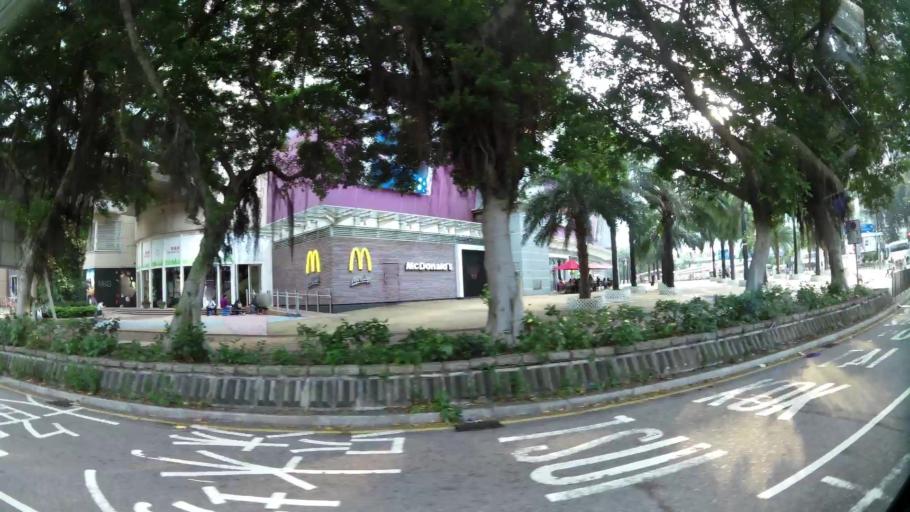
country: HK
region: Sham Shui Po
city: Sham Shui Po
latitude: 22.3178
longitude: 114.1630
